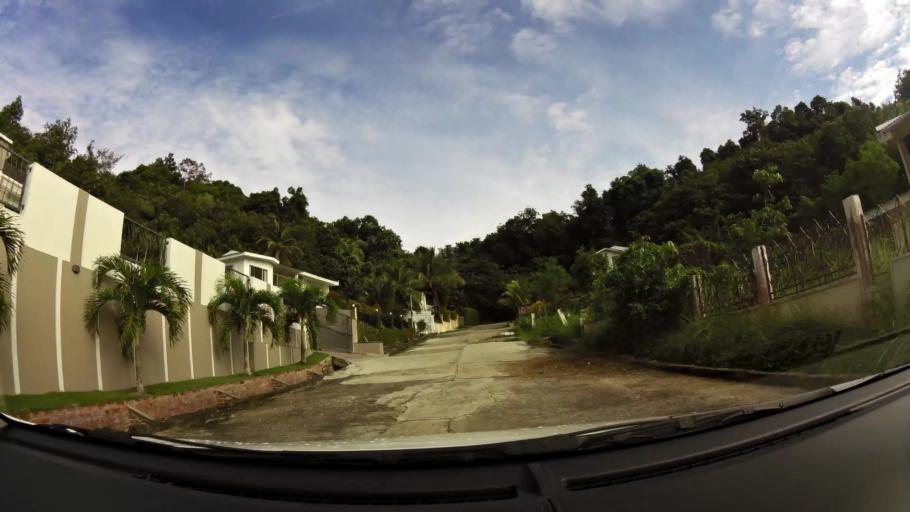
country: BN
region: Brunei and Muara
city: Bandar Seri Begawan
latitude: 4.8896
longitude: 114.9606
